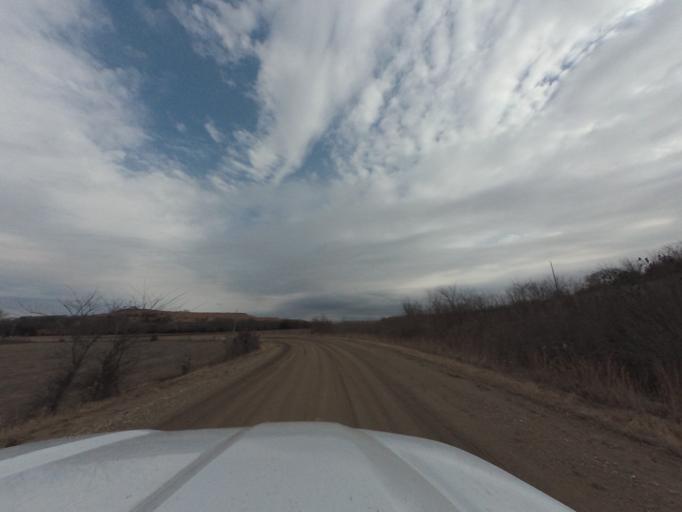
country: US
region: Kansas
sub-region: Chase County
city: Cottonwood Falls
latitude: 38.2844
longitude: -96.7332
